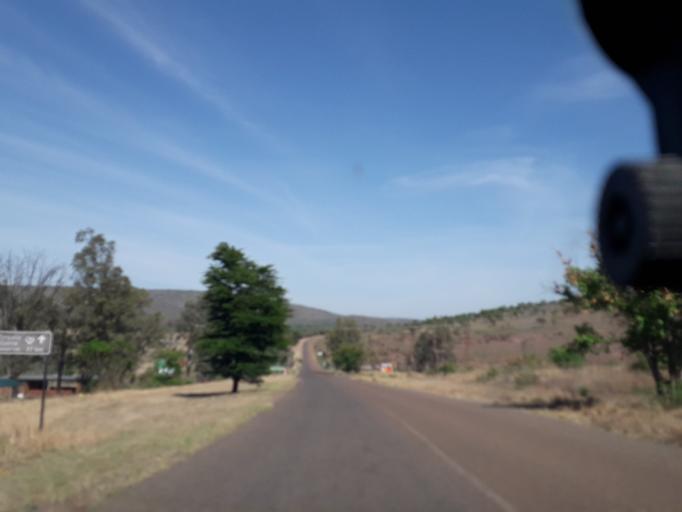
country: ZA
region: Limpopo
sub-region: Waterberg District Municipality
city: Warmbaths
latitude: -24.8311
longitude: 28.2248
